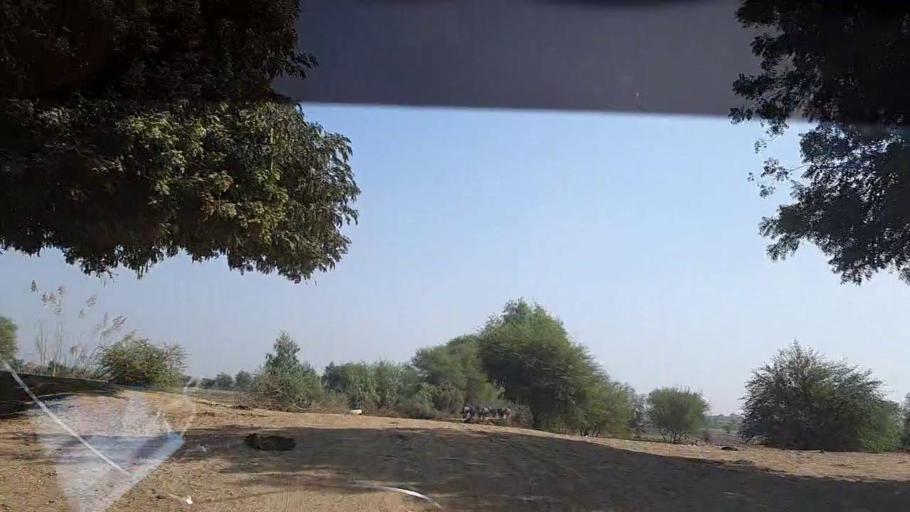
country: PK
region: Sindh
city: Naudero
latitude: 27.6470
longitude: 68.3692
